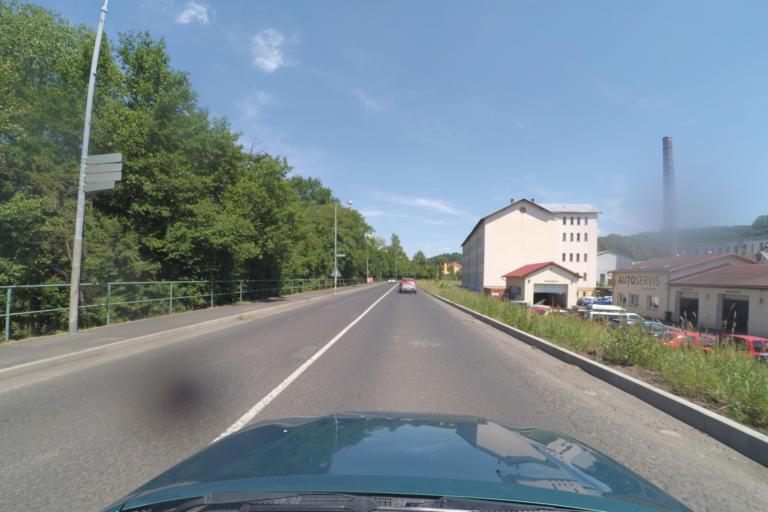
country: CZ
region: Ustecky
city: Benesov nad Ploucnici
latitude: 50.7401
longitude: 14.3060
